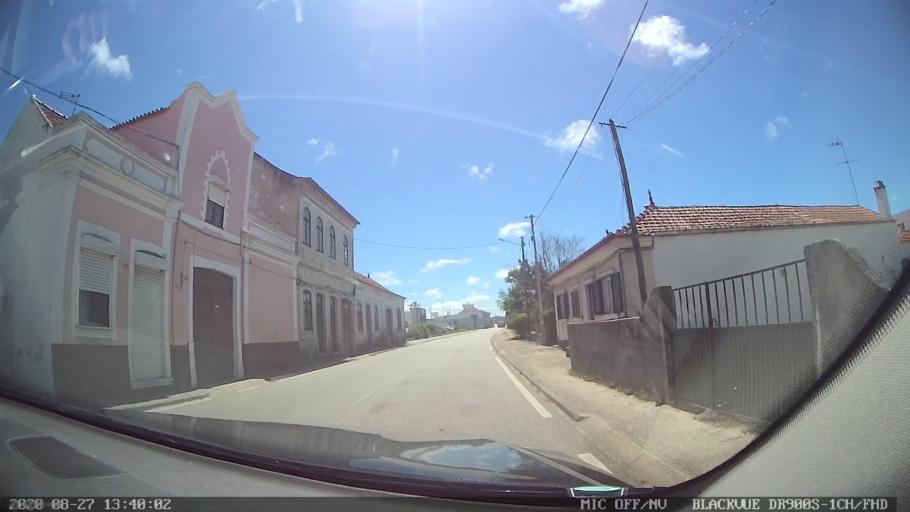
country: PT
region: Coimbra
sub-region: Mira
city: Mira
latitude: 40.4369
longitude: -8.7283
